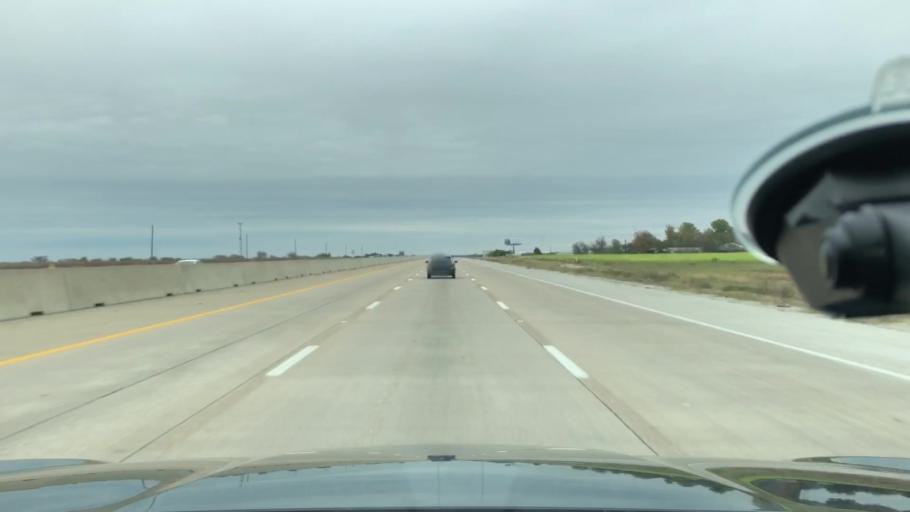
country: US
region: Texas
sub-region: Ellis County
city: Waxahachie
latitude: 32.3229
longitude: -96.8599
